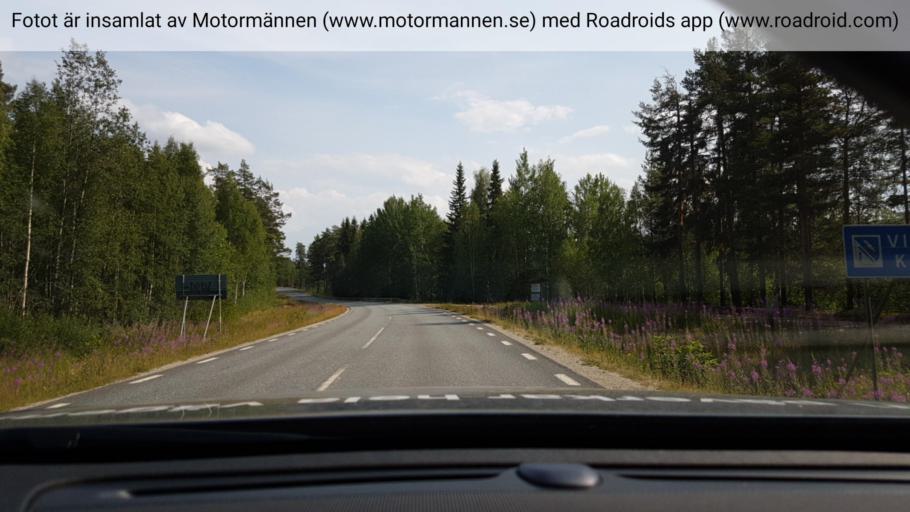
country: SE
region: Vaesterbotten
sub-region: Lycksele Kommun
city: Lycksele
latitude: 64.4314
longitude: 18.9755
